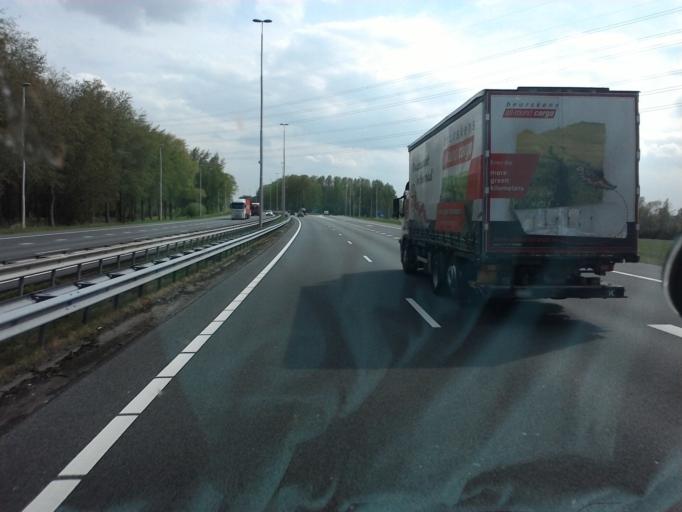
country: NL
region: Gelderland
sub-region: Gemeente Nijmegen
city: Lindenholt
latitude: 51.8287
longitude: 5.7725
